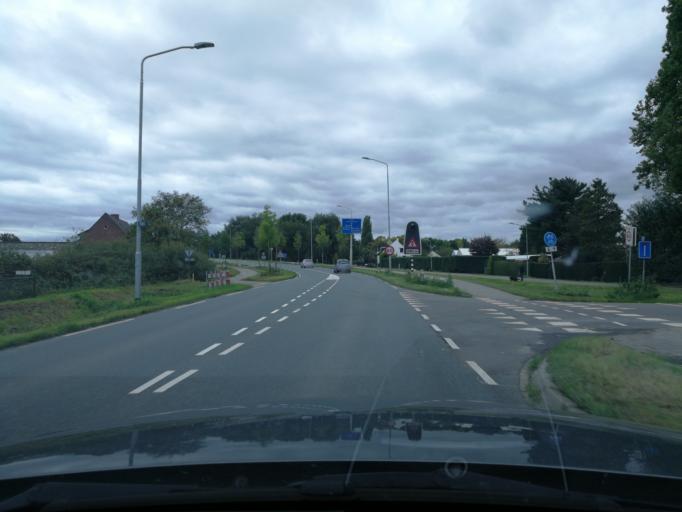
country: NL
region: Limburg
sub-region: Gemeente Venlo
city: Venlo
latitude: 51.3927
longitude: 6.2003
